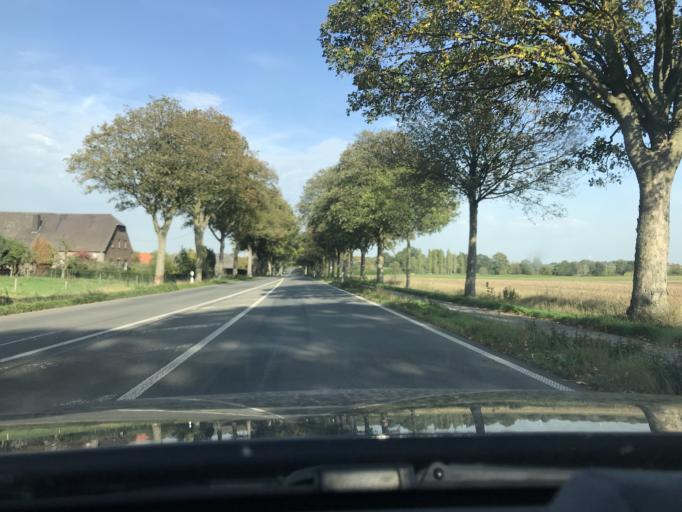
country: DE
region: North Rhine-Westphalia
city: Kalkar
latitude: 51.7205
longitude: 6.2628
